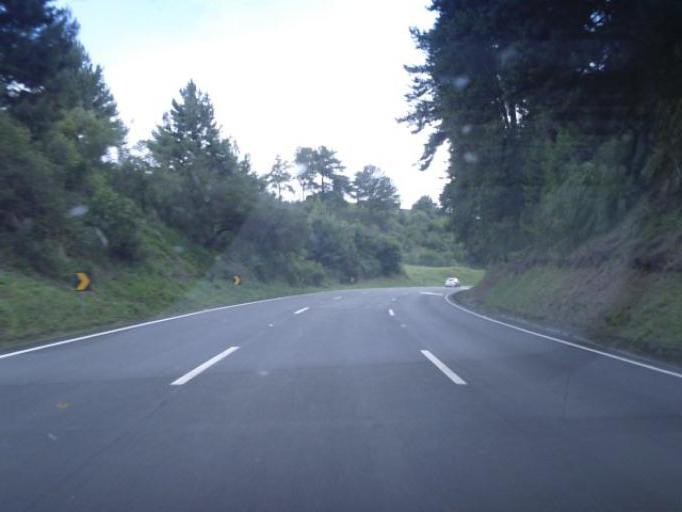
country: BR
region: Parana
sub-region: Campina Grande Do Sul
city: Campina Grande do Sul
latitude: -25.1898
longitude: -48.8845
